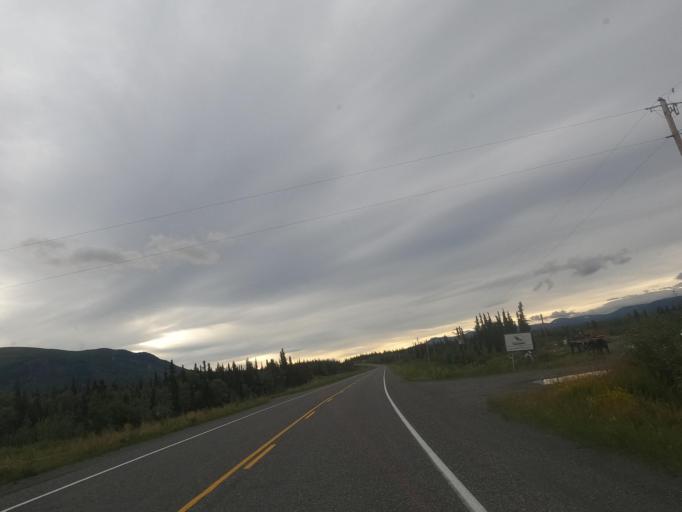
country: CA
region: Yukon
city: Haines Junction
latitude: 60.8585
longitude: -137.0595
